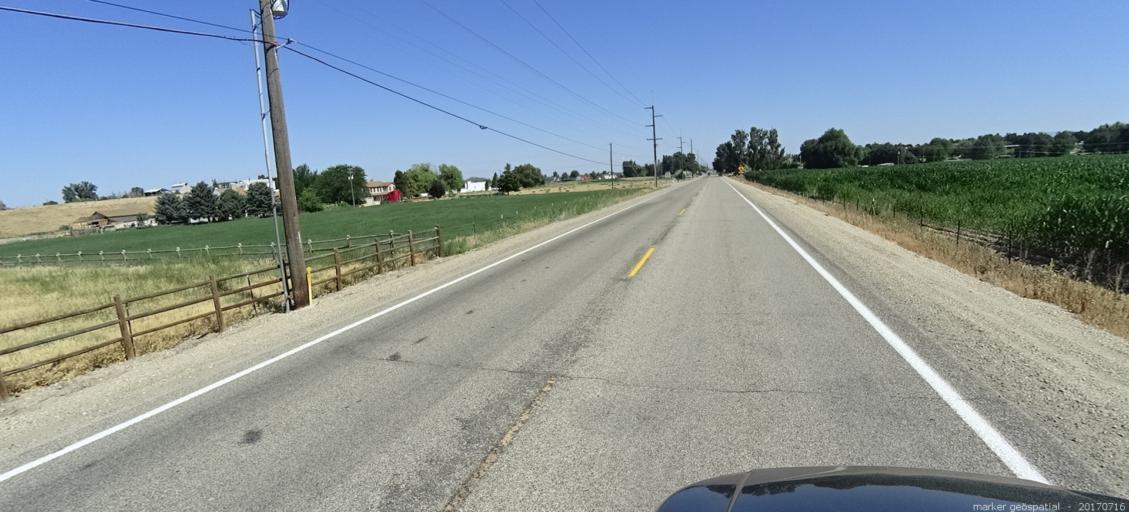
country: US
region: Idaho
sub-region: Ada County
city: Kuna
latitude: 43.5292
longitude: -116.3344
